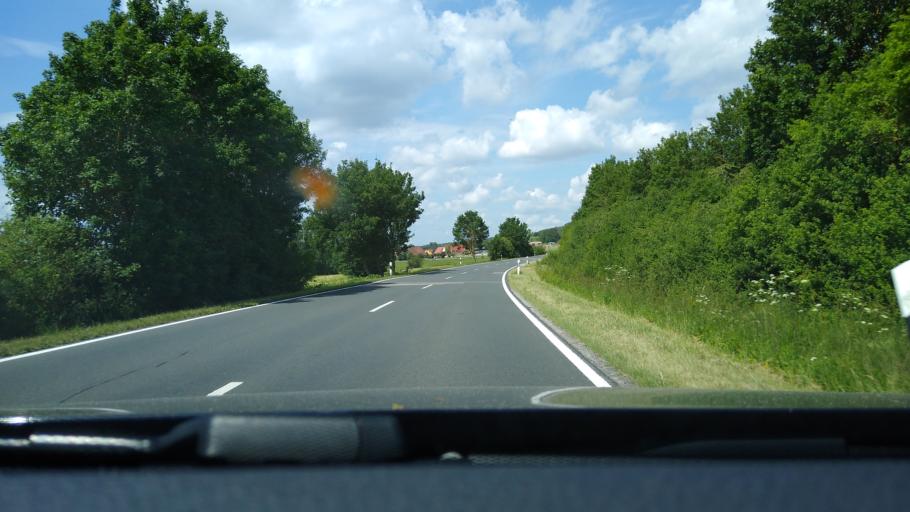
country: DE
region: Bavaria
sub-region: Regierungsbezirk Mittelfranken
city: Obernzenn
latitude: 49.4572
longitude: 10.5247
